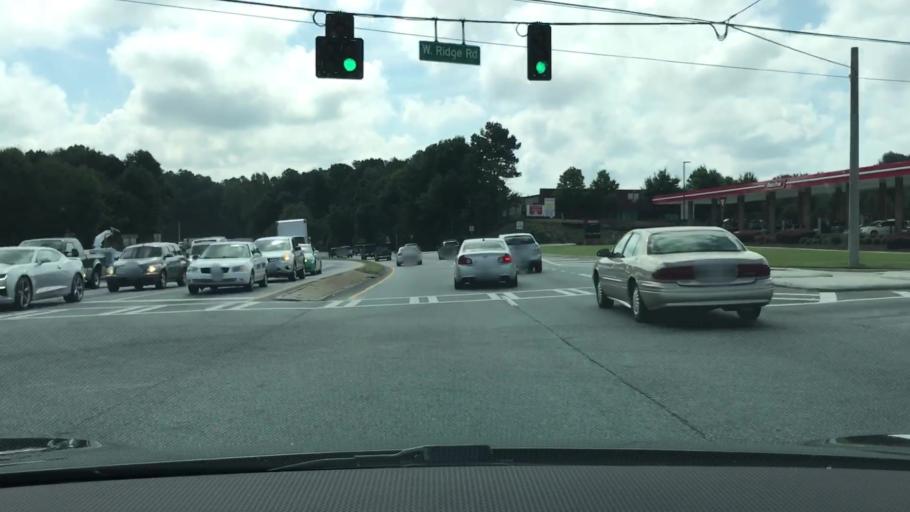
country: US
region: Georgia
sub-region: Hall County
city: Gainesville
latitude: 34.2876
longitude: -83.8114
